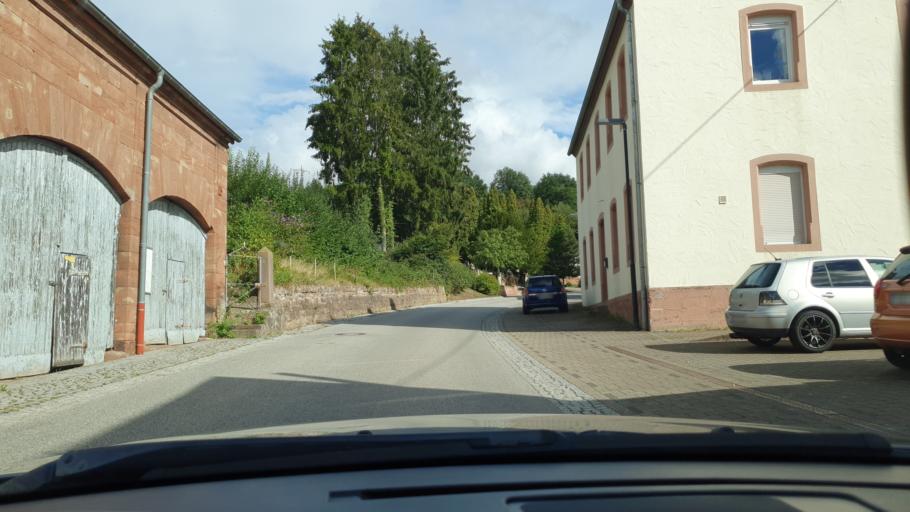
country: DE
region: Rheinland-Pfalz
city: Wallhalben
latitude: 49.3155
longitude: 7.5250
